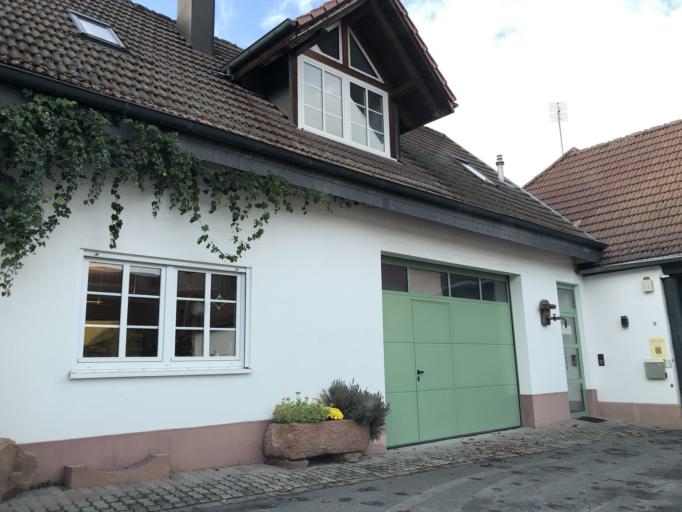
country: DE
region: Rheinland-Pfalz
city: Siebeldingen
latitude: 49.2094
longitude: 8.0463
